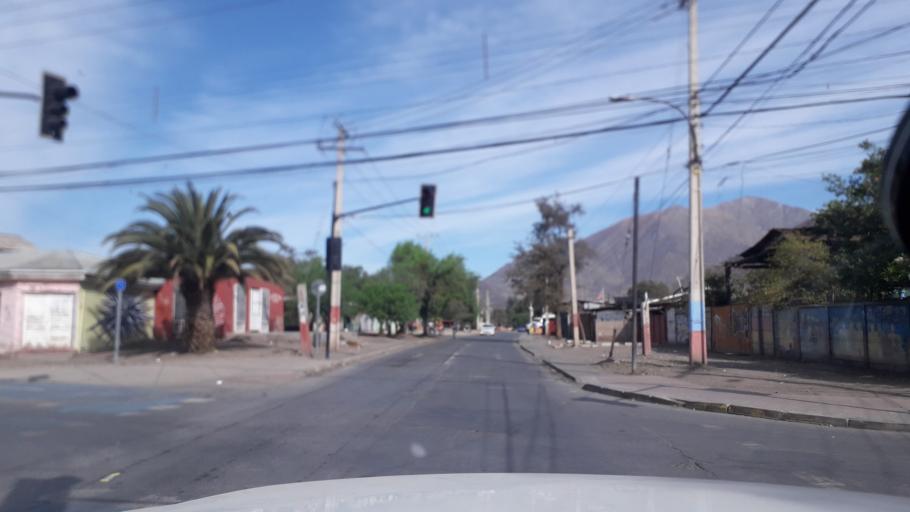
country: CL
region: Valparaiso
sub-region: Provincia de San Felipe
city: San Felipe
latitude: -32.7477
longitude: -70.7340
